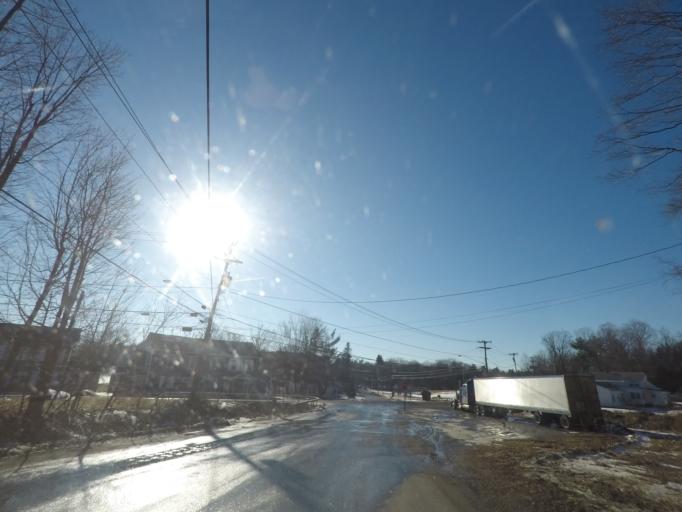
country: US
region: New York
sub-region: Rensselaer County
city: Averill Park
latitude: 42.6305
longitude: -73.5303
